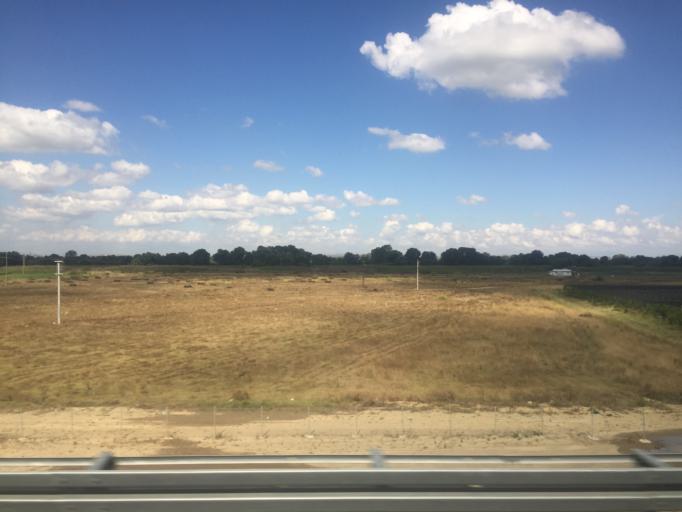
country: TR
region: Bursa
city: Tatkavakli
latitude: 40.1183
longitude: 28.2789
